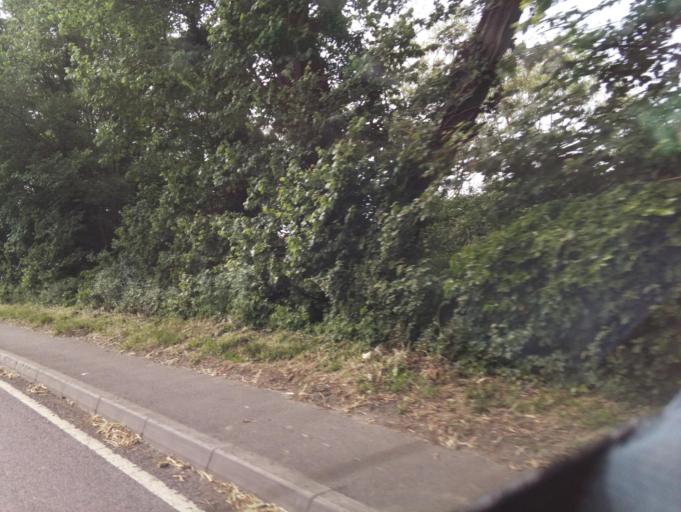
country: GB
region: England
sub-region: Worcestershire
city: Badsey
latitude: 52.0916
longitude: -1.9077
